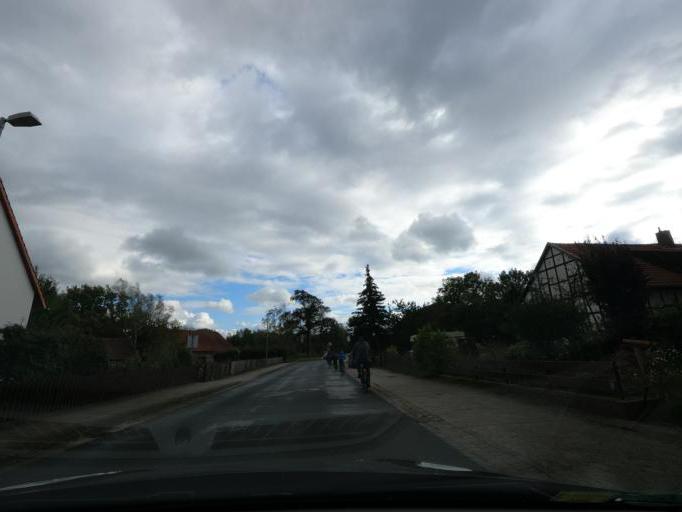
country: DE
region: Lower Saxony
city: Klein Schwulper
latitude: 52.3346
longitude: 10.4383
